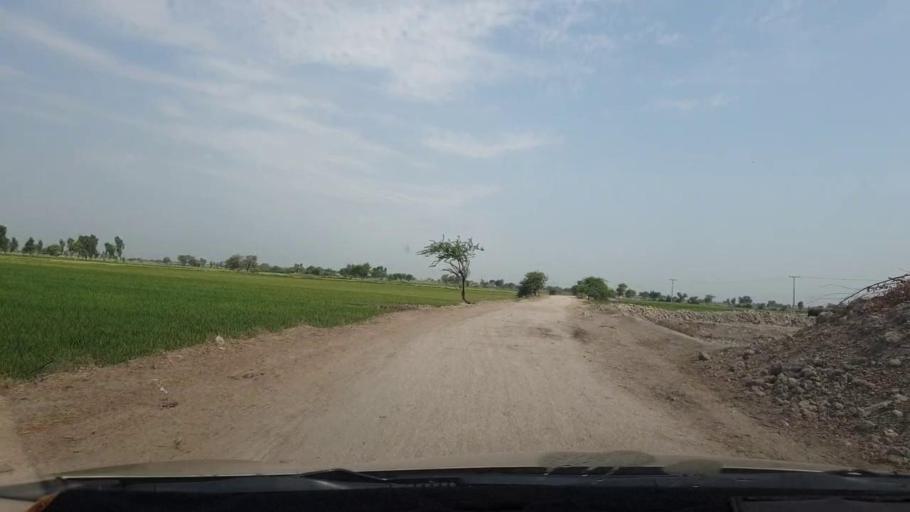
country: PK
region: Sindh
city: Larkana
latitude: 27.6707
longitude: 68.2211
